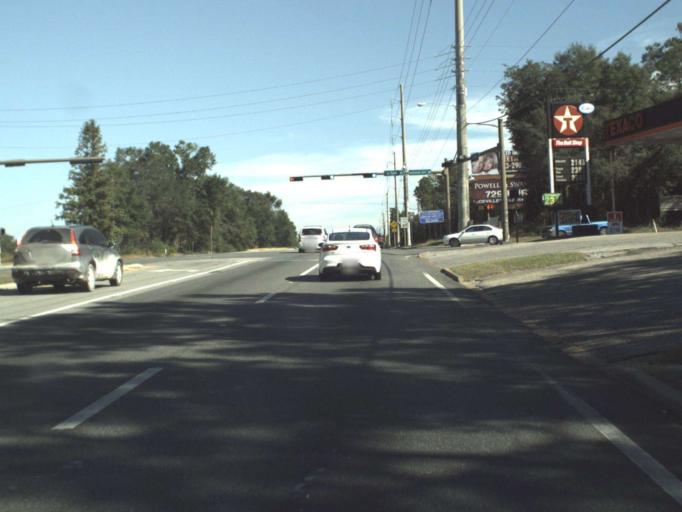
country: US
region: Florida
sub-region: Okaloosa County
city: Niceville
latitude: 30.5145
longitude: -86.4597
